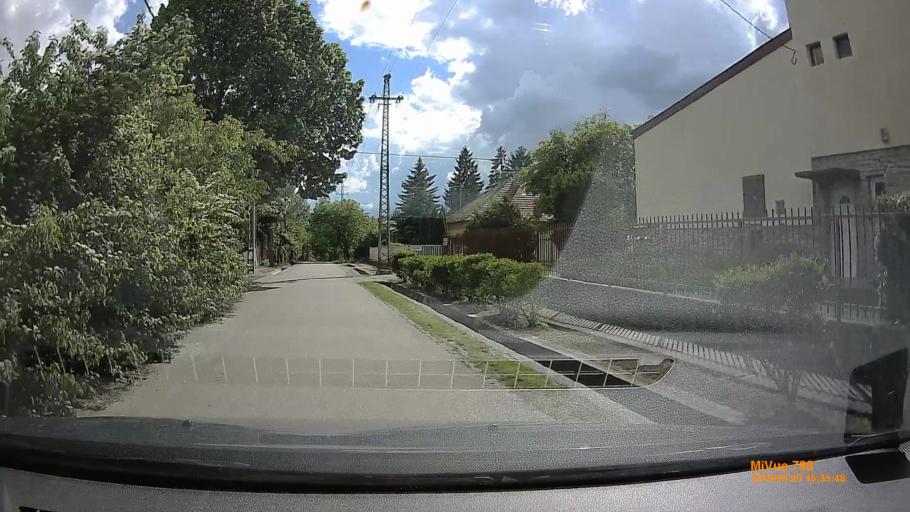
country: HU
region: Budapest
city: Budapest XVII. keruelet
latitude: 47.4895
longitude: 19.2520
